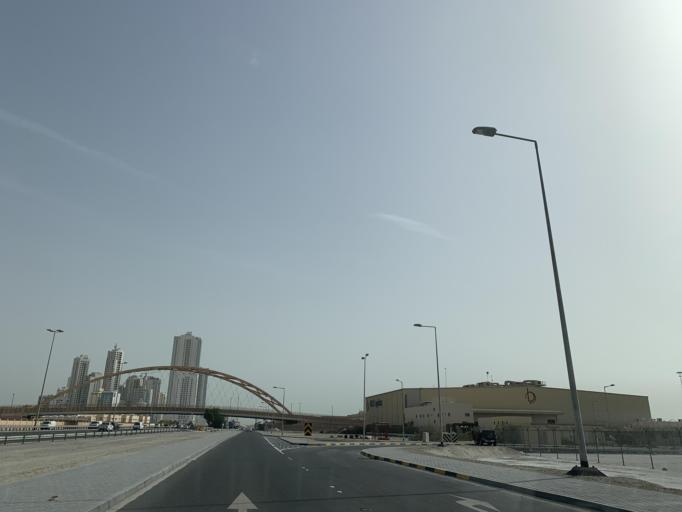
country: BH
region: Manama
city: Manama
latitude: 26.2055
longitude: 50.6126
